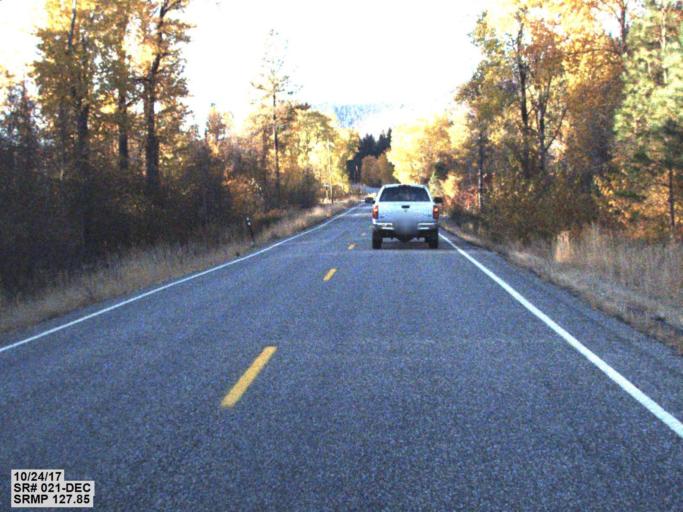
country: US
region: Washington
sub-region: Okanogan County
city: Coulee Dam
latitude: 48.2309
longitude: -118.7014
